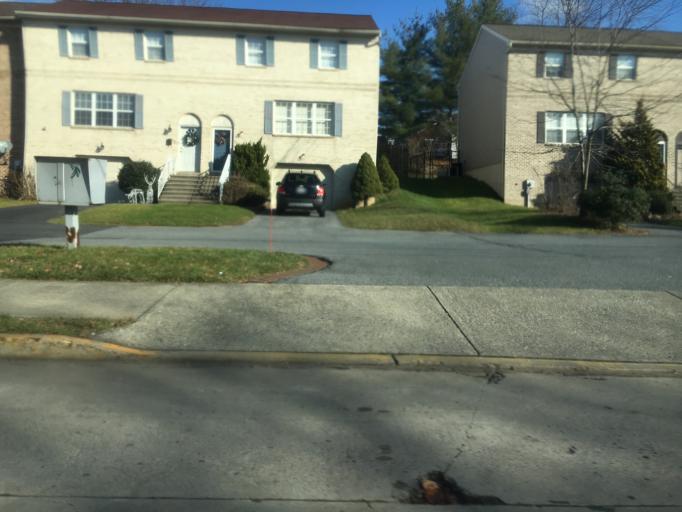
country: US
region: Pennsylvania
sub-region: Lehigh County
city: Coplay
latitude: 40.6742
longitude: -75.4854
